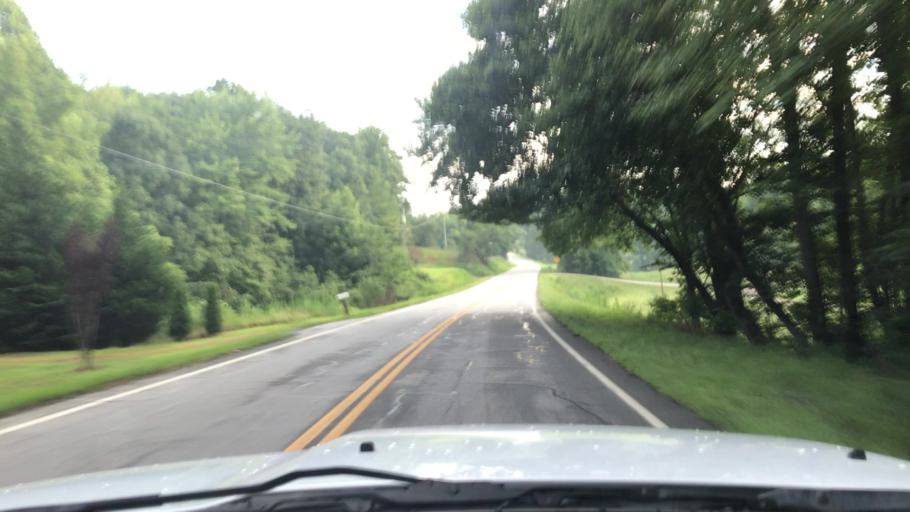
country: US
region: Georgia
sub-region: Fannin County
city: Blue Ridge
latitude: 34.9520
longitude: -84.2334
